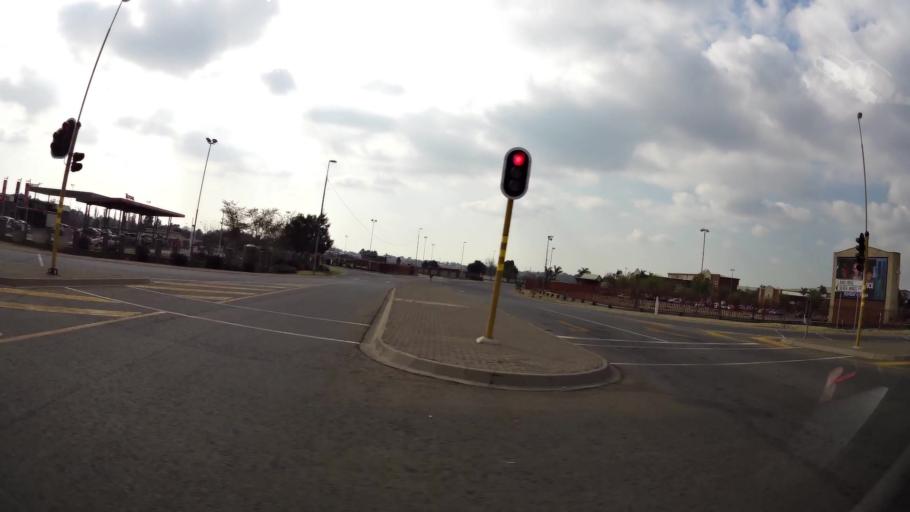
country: ZA
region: Gauteng
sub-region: Ekurhuleni Metropolitan Municipality
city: Benoni
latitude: -26.1329
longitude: 28.2673
